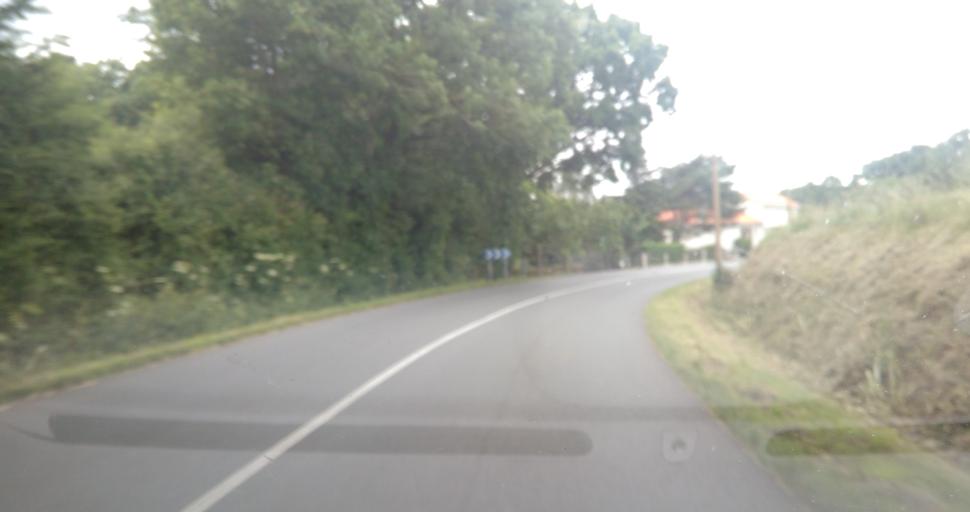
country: FR
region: Pays de la Loire
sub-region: Departement de la Vendee
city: La Chaize-le-Vicomte
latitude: 46.6792
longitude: -1.2974
